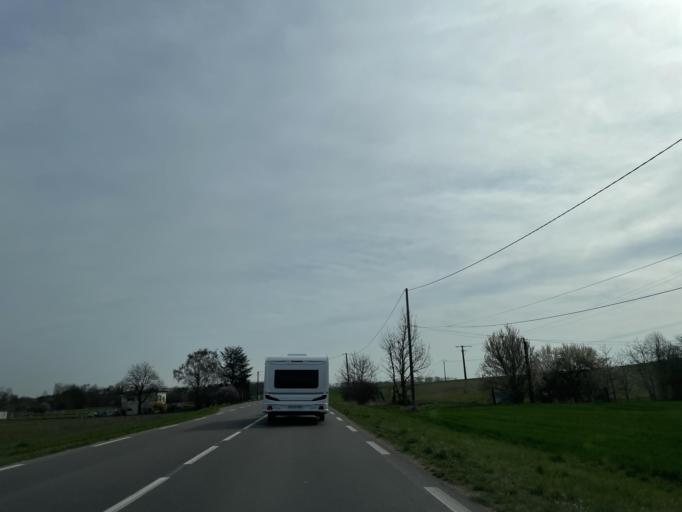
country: FR
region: Champagne-Ardenne
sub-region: Departement de l'Aube
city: Romilly-sur-Seine
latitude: 48.5138
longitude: 3.6720
